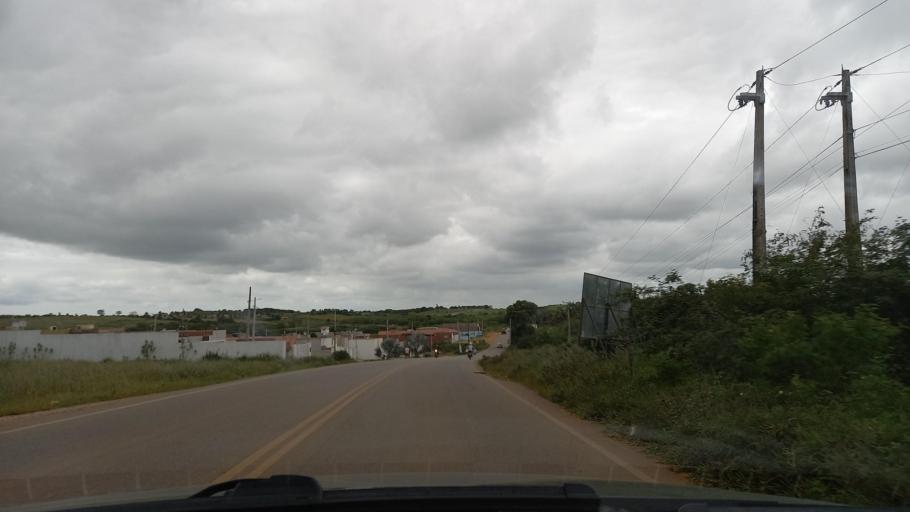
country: BR
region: Sergipe
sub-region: Caninde De Sao Francisco
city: Caninde de Sao Francisco
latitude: -9.6837
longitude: -37.7873
